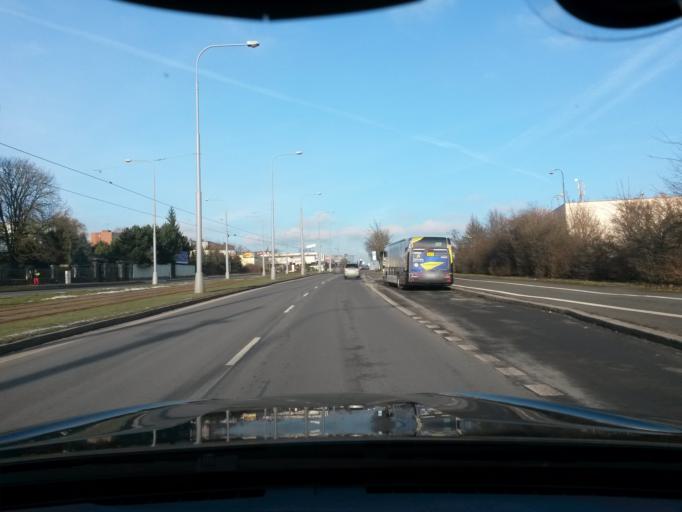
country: CZ
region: Plzensky
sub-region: Okres Plzen-Mesto
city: Pilsen
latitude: 49.7644
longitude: 13.3718
